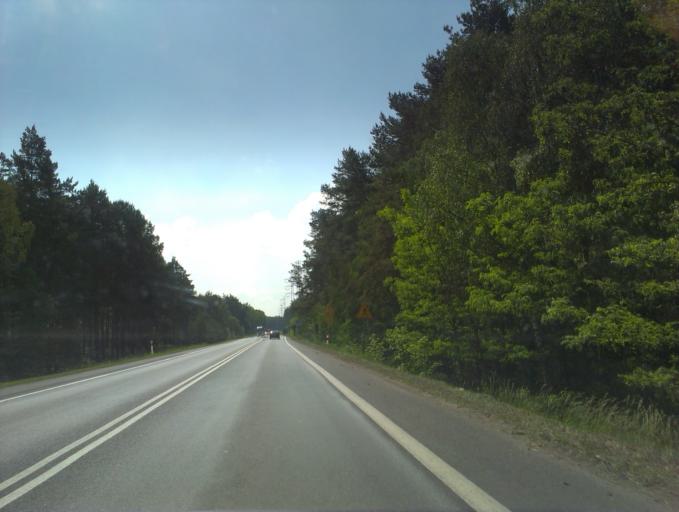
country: PL
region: Greater Poland Voivodeship
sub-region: Powiat pilski
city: Pila
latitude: 53.1675
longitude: 16.7820
